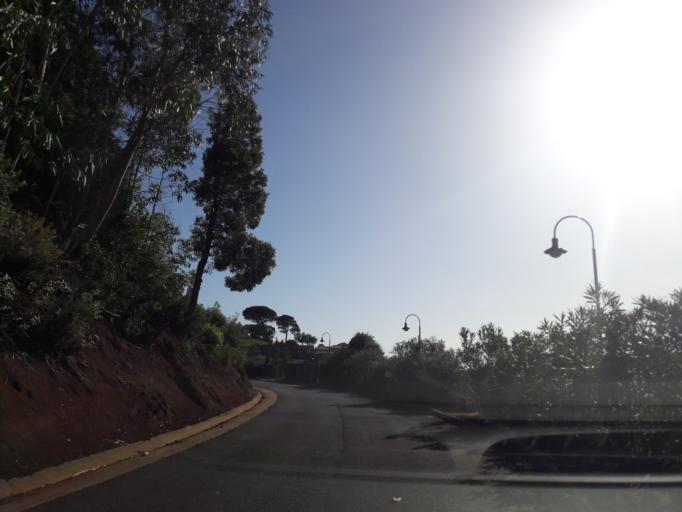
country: PT
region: Madeira
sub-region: Funchal
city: Nossa Senhora do Monte
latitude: 32.6558
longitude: -16.8719
